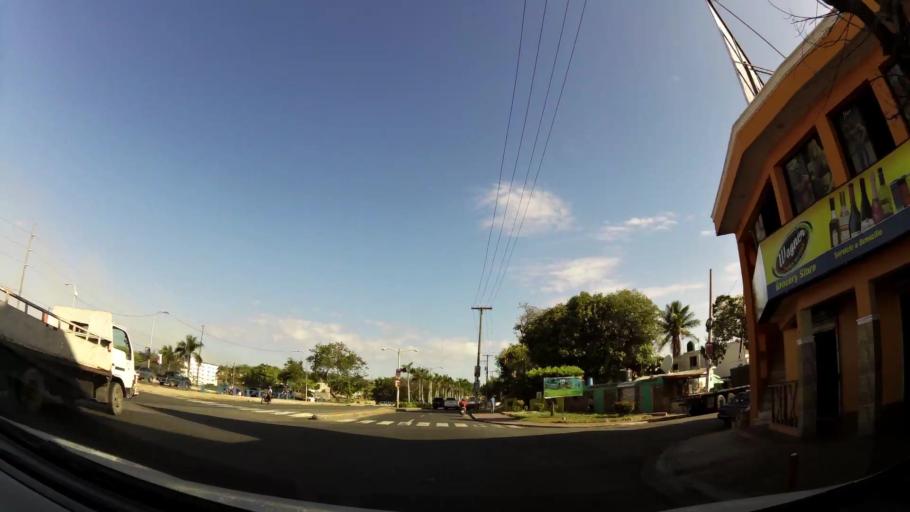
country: DO
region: Nacional
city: San Carlos
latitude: 18.4761
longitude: -69.8779
